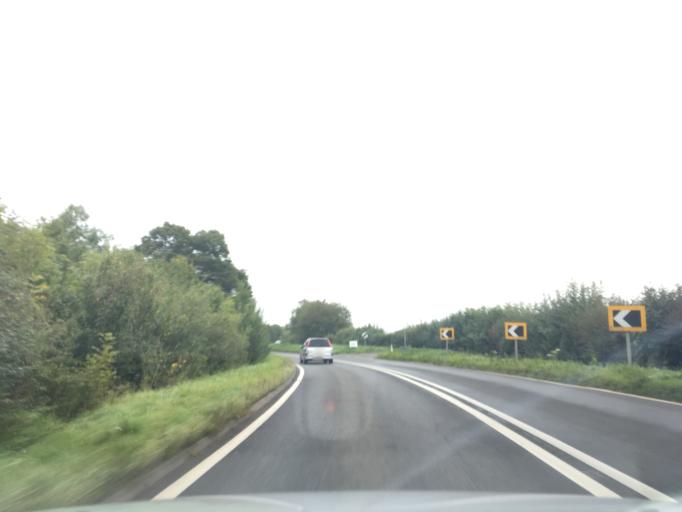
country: GB
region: England
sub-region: Oxfordshire
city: Claydon
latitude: 52.1062
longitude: -1.2938
